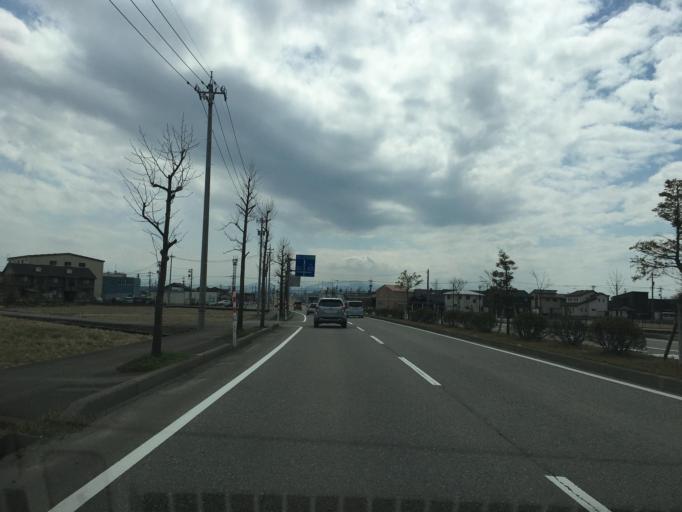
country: JP
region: Toyama
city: Kuragaki-kosugi
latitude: 36.7225
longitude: 137.1201
